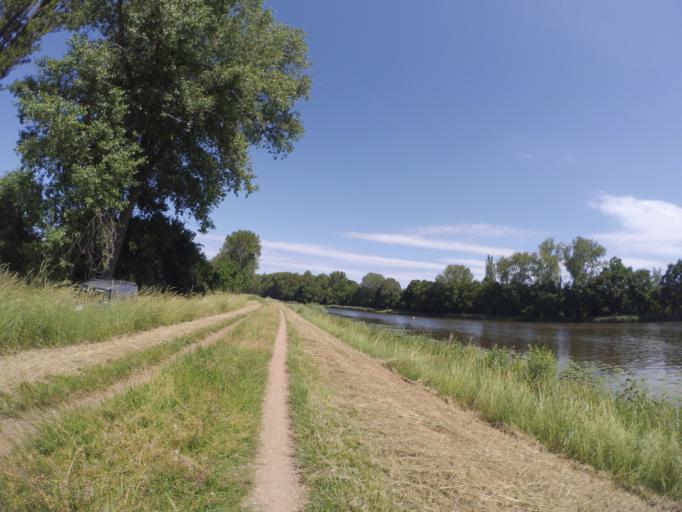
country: CZ
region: Central Bohemia
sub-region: Okres Nymburk
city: Sadska
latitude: 50.1694
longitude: 14.9972
